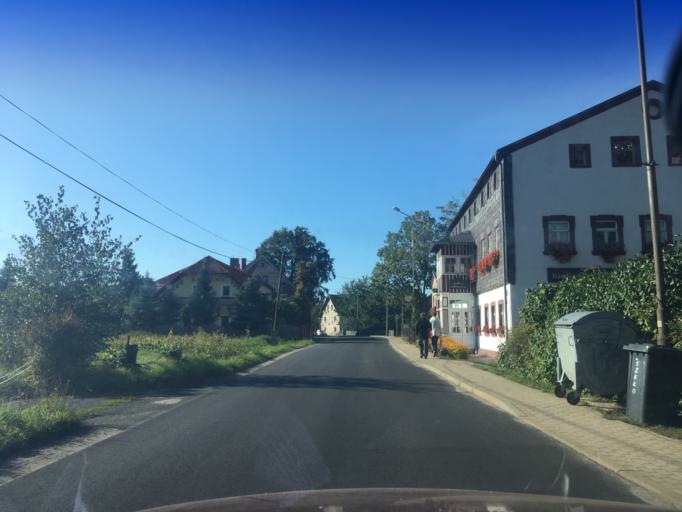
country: PL
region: Lower Silesian Voivodeship
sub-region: Powiat lubanski
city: Swieradow-Zdroj
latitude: 50.9293
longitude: 15.3055
